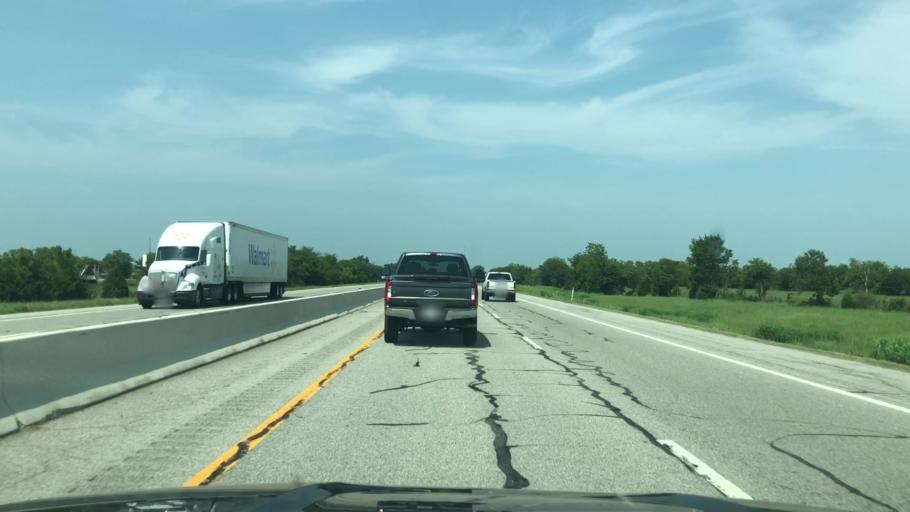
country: US
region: Oklahoma
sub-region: Ottawa County
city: Fairland
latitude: 36.7808
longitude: -94.8897
